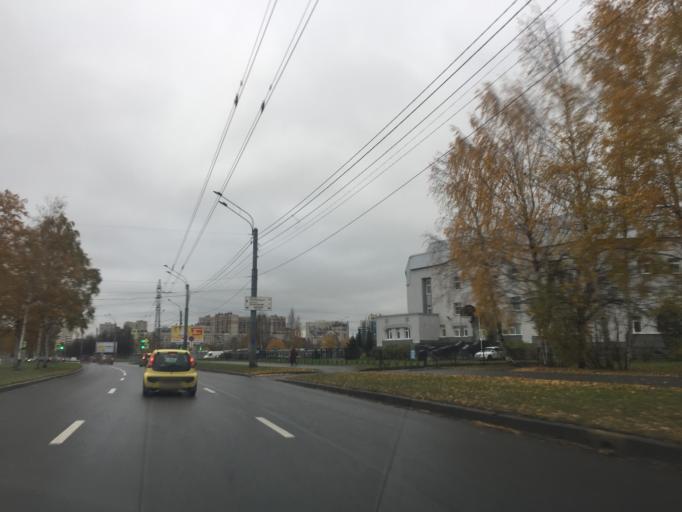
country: RU
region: Leningrad
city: Akademicheskoe
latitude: 60.0263
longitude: 30.3862
